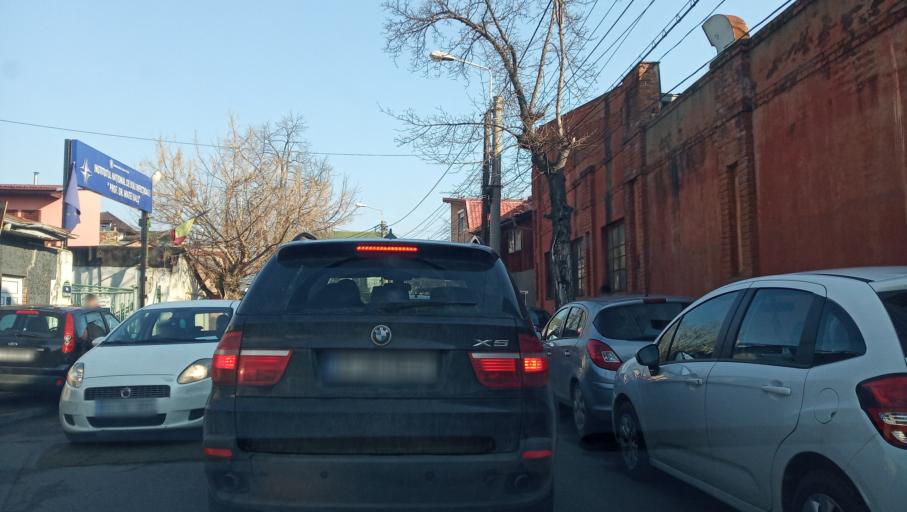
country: RO
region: Bucuresti
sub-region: Municipiul Bucuresti
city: Bucharest
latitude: 44.4555
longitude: 26.1158
